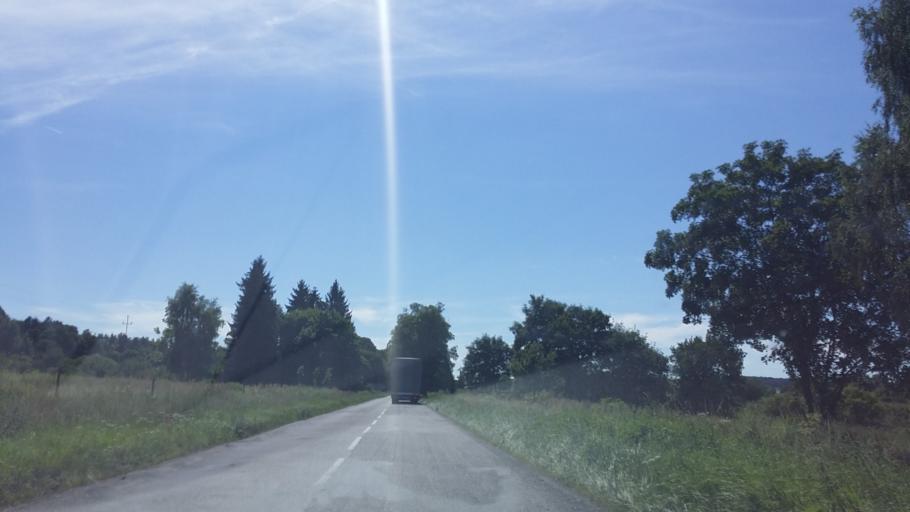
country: PL
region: West Pomeranian Voivodeship
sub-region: Powiat lobeski
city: Lobez
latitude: 53.6486
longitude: 15.6395
